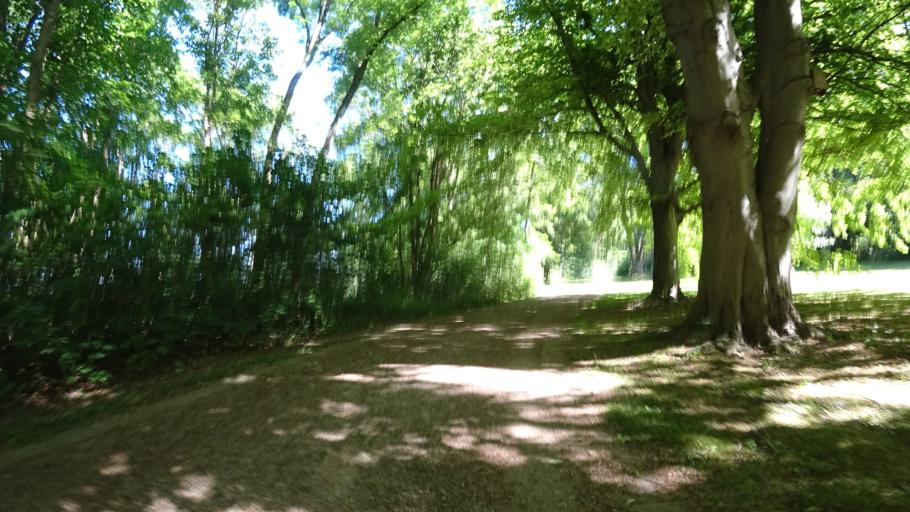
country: DE
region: North Rhine-Westphalia
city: Erwitte
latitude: 51.6344
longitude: 8.3531
